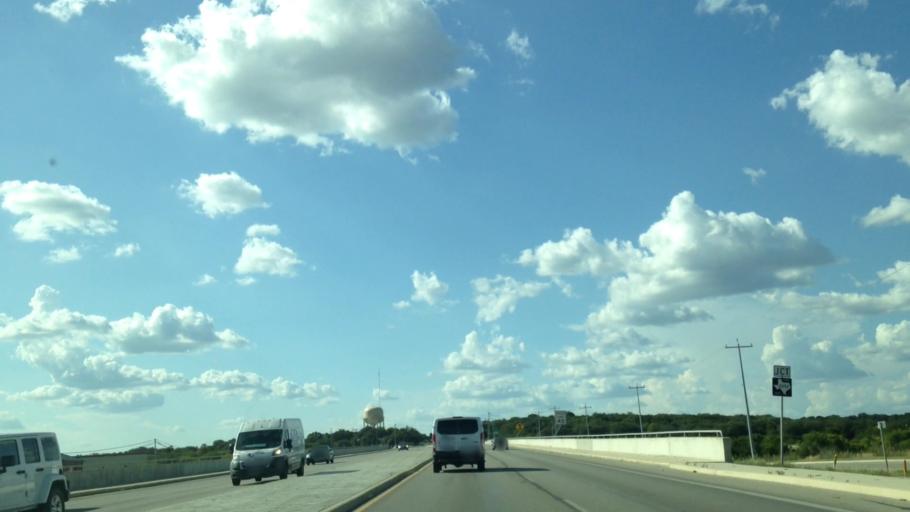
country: US
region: Texas
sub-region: Comal County
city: Garden Ridge
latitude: 29.6191
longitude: -98.2868
